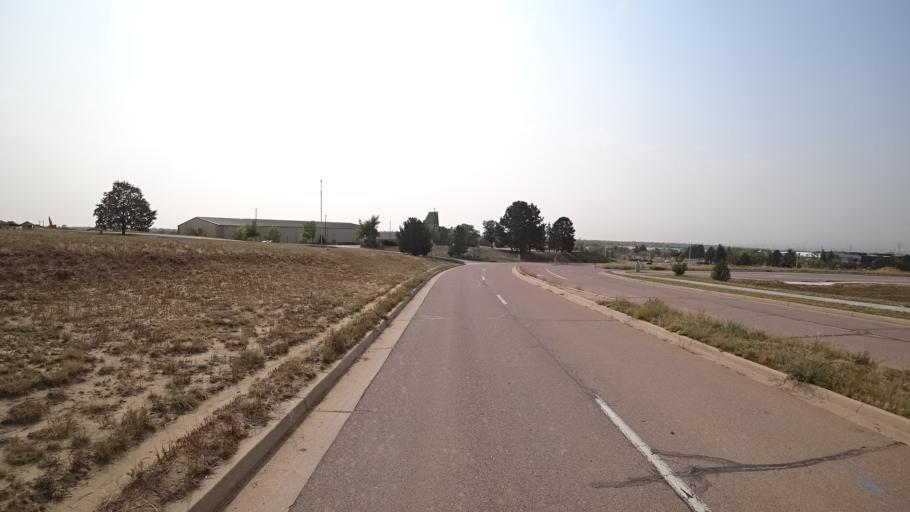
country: US
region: Colorado
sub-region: El Paso County
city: Stratmoor
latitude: 38.8156
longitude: -104.7527
